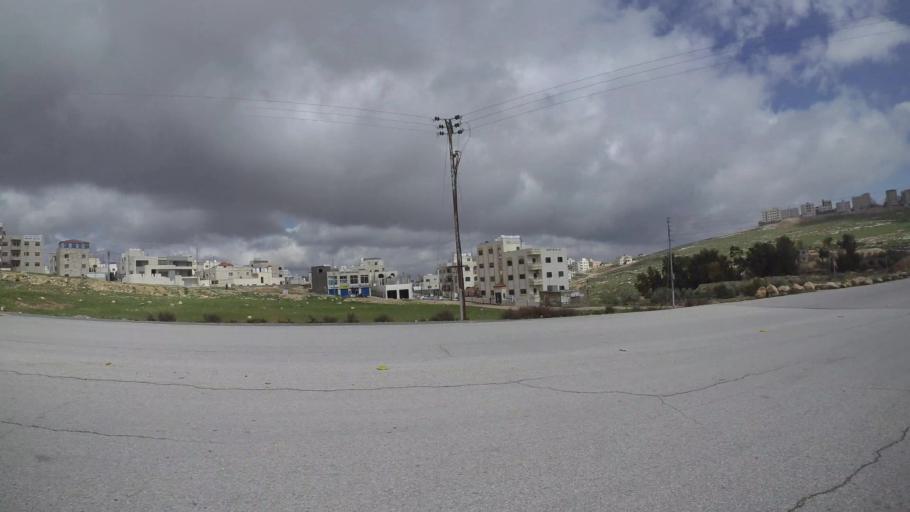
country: JO
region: Amman
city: Al Jubayhah
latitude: 32.0706
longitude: 35.8841
